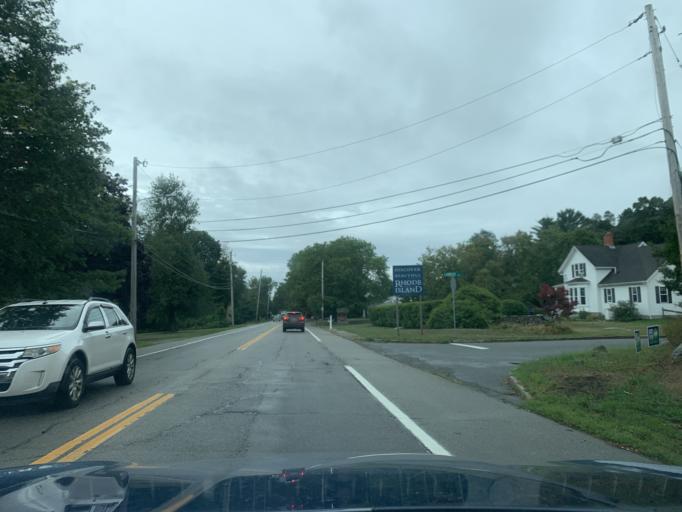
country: US
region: Rhode Island
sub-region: Bristol County
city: Warren
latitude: 41.7563
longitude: -71.2709
